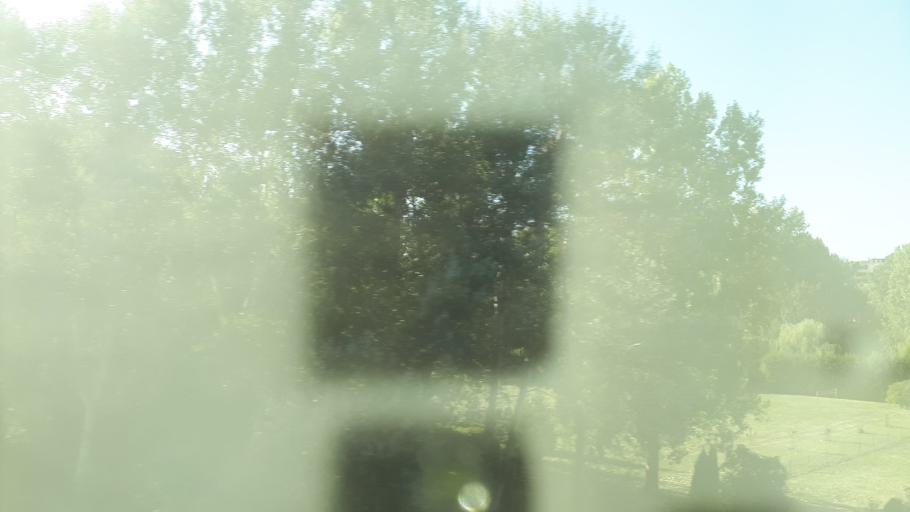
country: FR
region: Centre
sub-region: Departement d'Indre-et-Loire
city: Vouvray
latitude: 47.4064
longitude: 0.8133
